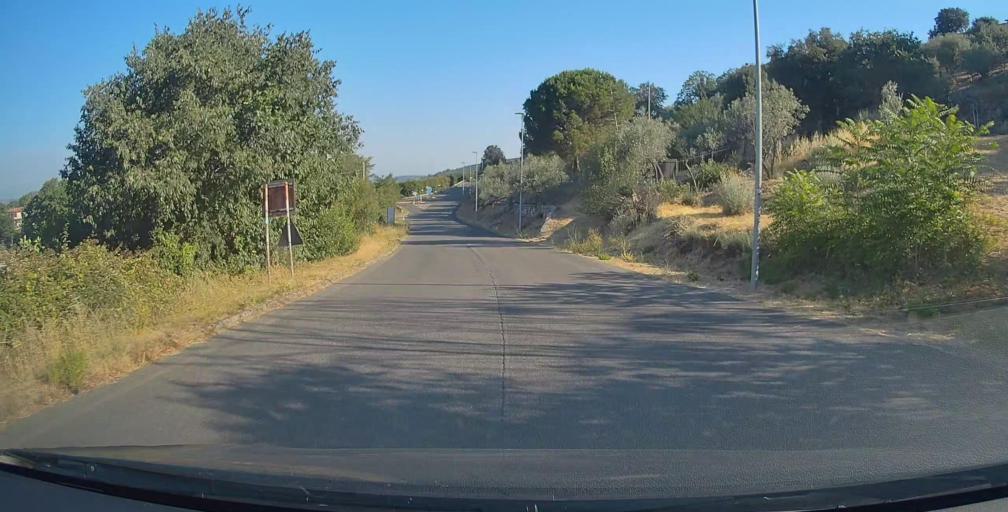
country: IT
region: Umbria
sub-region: Provincia di Terni
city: Calvi dell'Umbria
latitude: 42.4057
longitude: 12.5656
